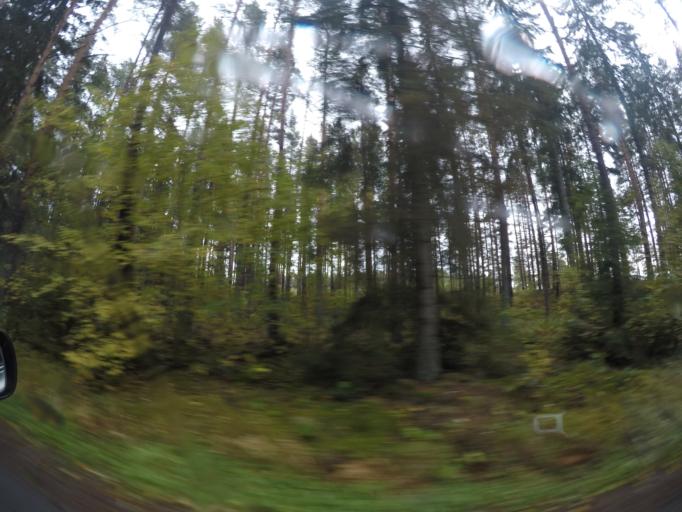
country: SE
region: Soedermanland
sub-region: Eskilstuna Kommun
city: Kvicksund
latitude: 59.3332
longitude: 16.2968
